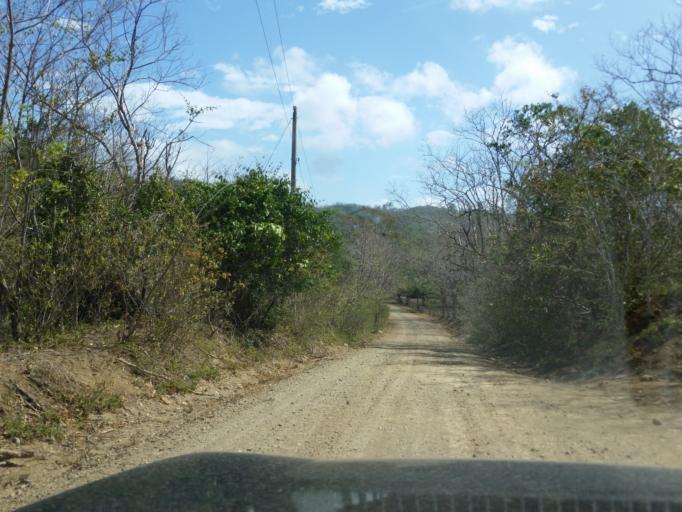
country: CR
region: Guanacaste
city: La Cruz
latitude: 11.1089
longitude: -85.7453
